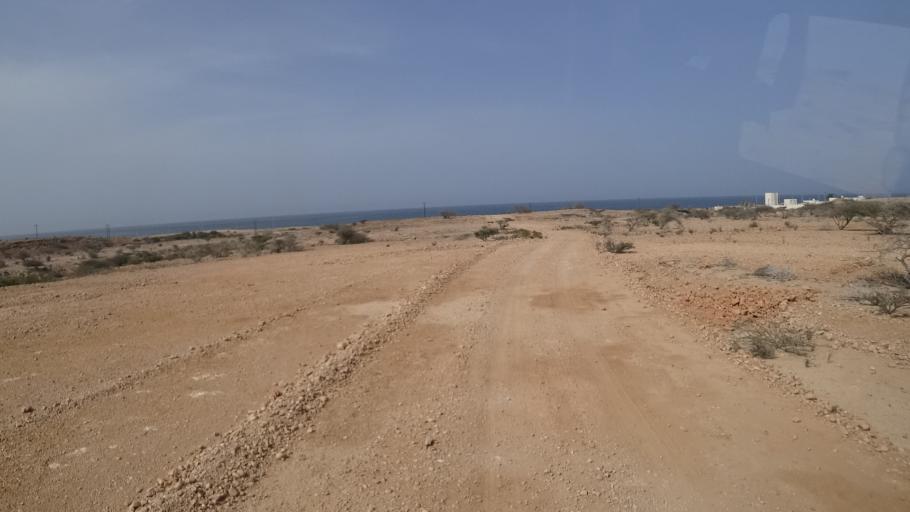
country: OM
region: Ash Sharqiyah
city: Sur
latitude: 22.9932
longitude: 59.1265
